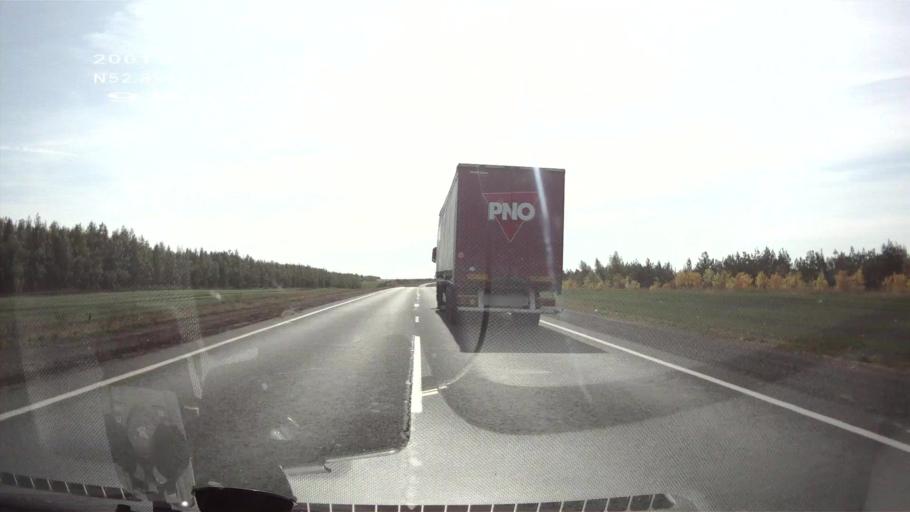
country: RU
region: Samara
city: Syzran'
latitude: 52.8933
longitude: 48.2952
